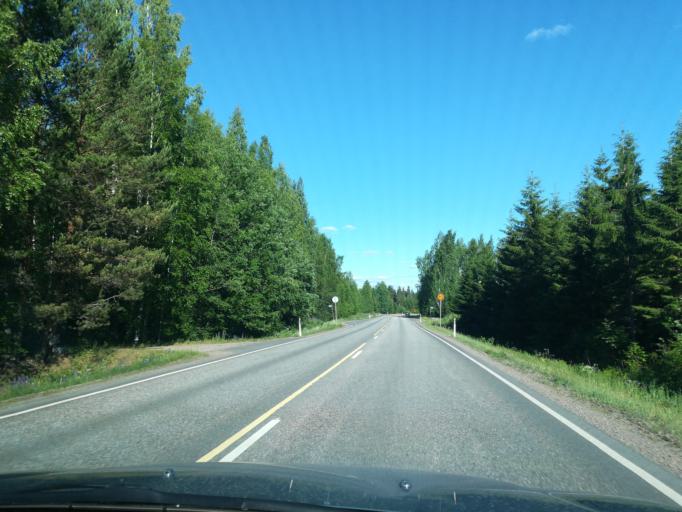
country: FI
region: South Karelia
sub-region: Imatra
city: Ruokolahti
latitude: 61.3529
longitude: 28.7265
